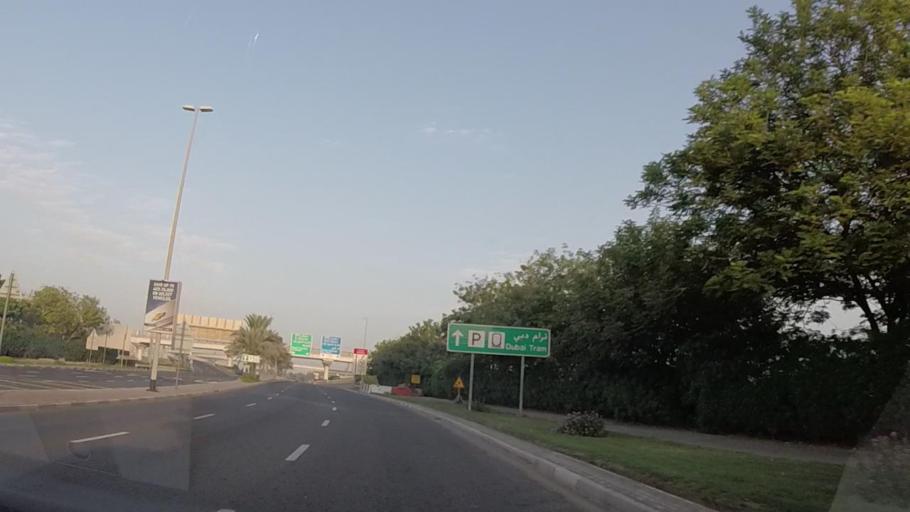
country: AE
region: Dubai
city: Dubai
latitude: 25.0540
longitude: 55.1216
